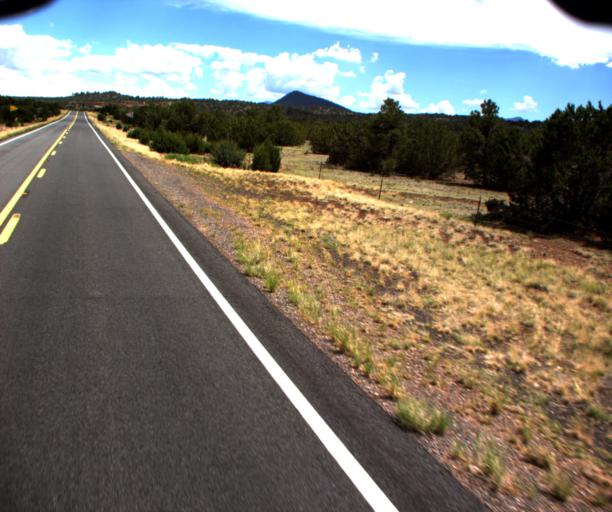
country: US
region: Arizona
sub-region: Coconino County
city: Parks
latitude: 35.5673
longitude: -111.9172
